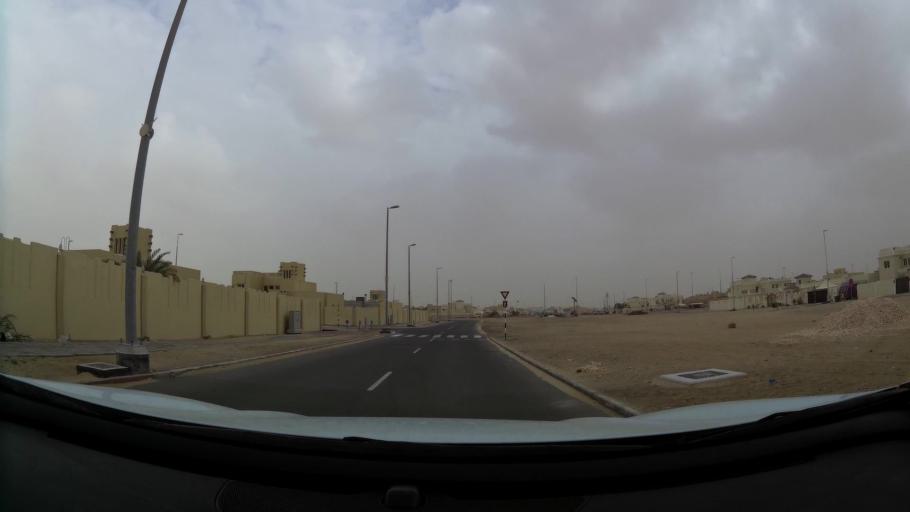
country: AE
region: Abu Dhabi
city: Abu Dhabi
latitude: 24.4492
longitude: 54.7188
